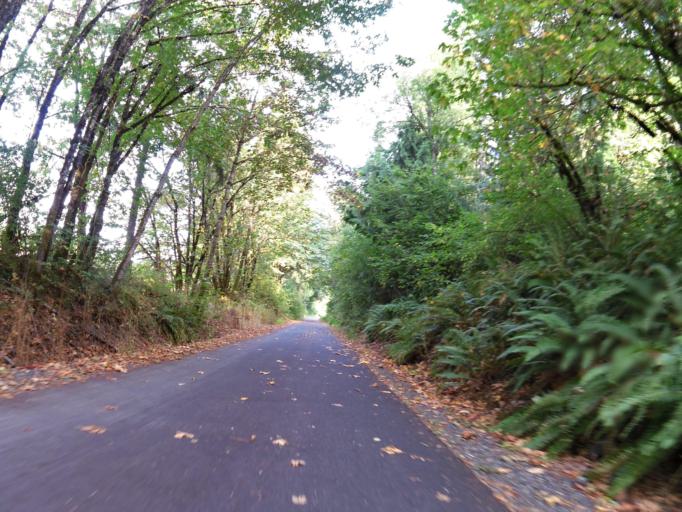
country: US
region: Washington
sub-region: Thurston County
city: Lacey
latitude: 46.9791
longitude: -122.8189
